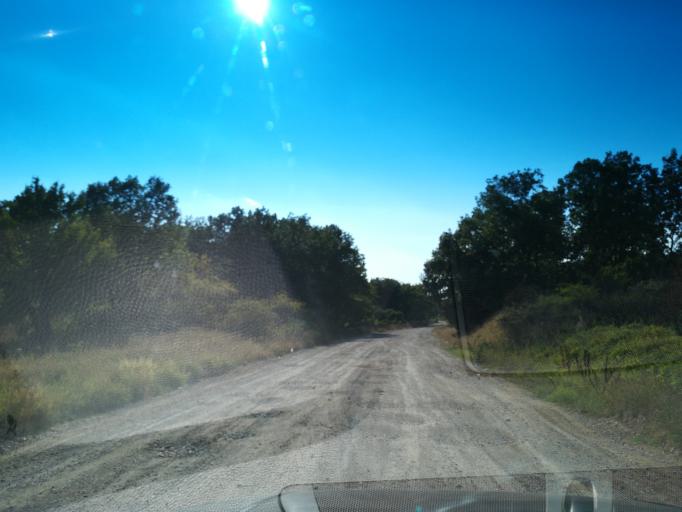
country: BG
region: Khaskovo
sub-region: Obshtina Mineralni Bani
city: Mineralni Bani
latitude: 41.9716
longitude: 25.3339
